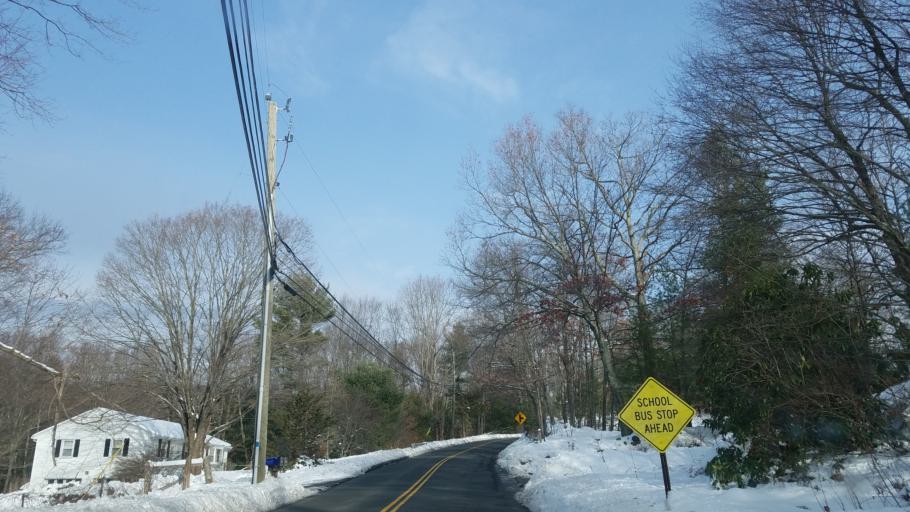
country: US
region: Connecticut
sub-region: Hartford County
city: Canton Valley
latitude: 41.8382
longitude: -72.9048
